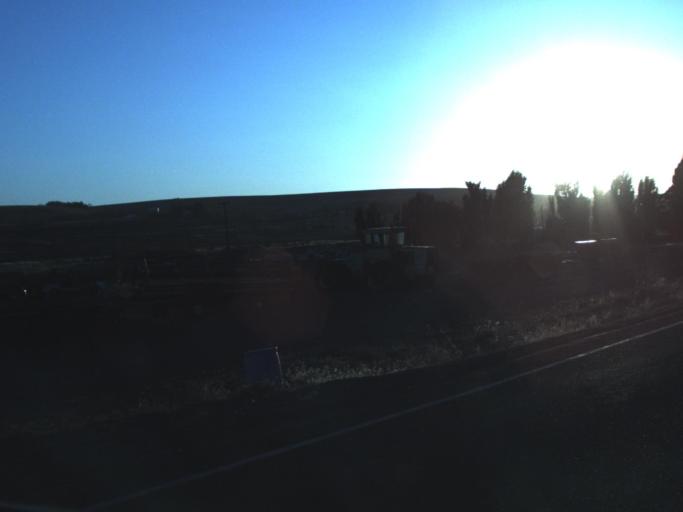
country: US
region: Washington
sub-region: Adams County
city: Ritzville
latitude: 46.9712
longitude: -118.6051
